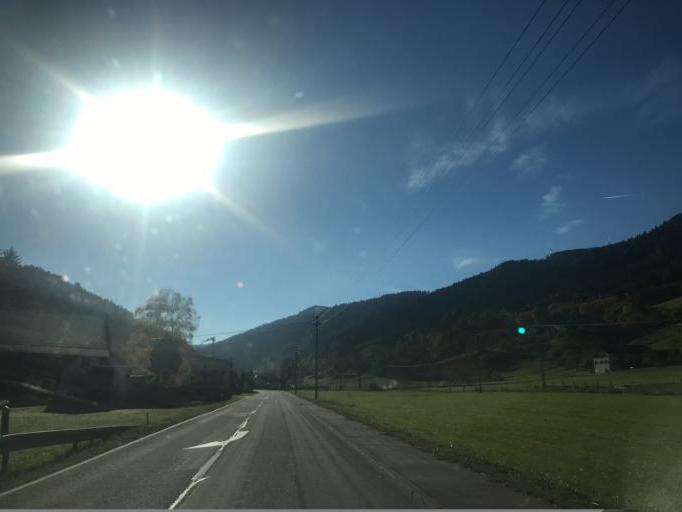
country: DE
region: Baden-Wuerttemberg
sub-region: Freiburg Region
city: Gutenbach
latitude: 48.0699
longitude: 8.0988
